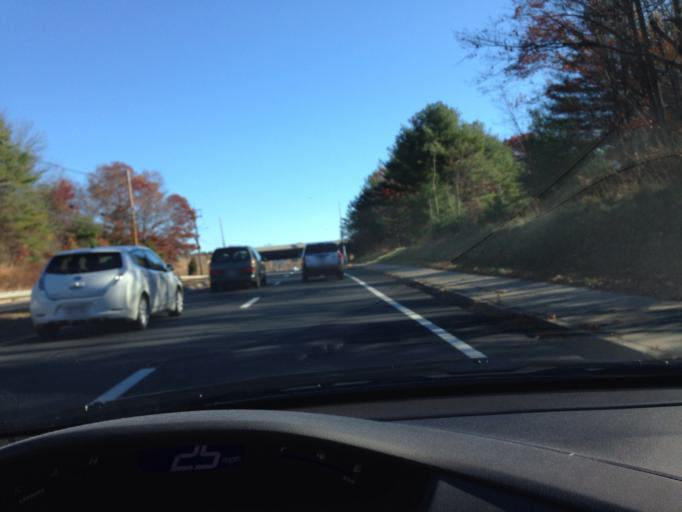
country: US
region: Massachusetts
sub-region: Middlesex County
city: Bedford
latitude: 42.5016
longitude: -71.2457
